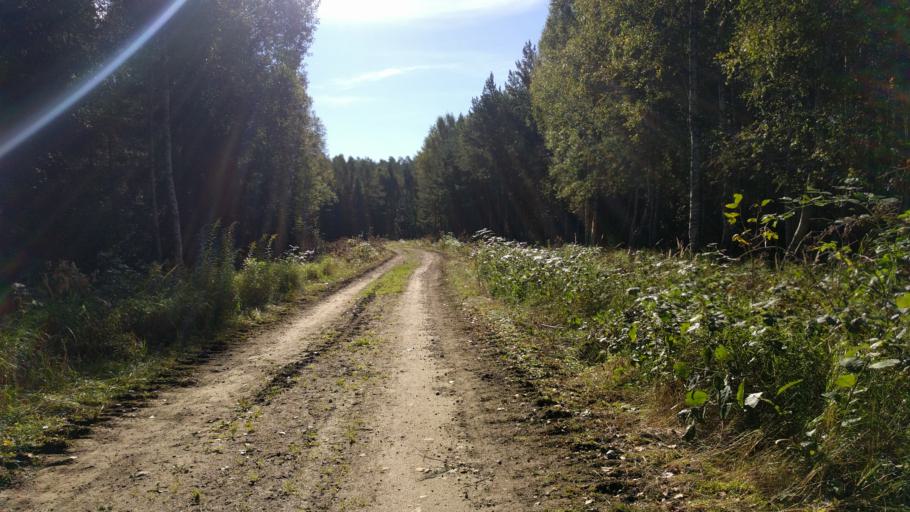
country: SE
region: Stockholm
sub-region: Vallentuna Kommun
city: Vallentuna
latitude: 59.4945
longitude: 18.1116
